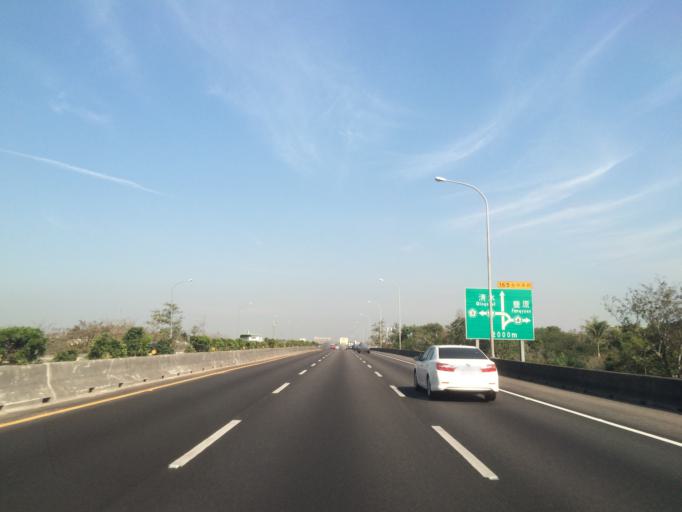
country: TW
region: Taiwan
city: Fengyuan
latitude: 24.2500
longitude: 120.6904
